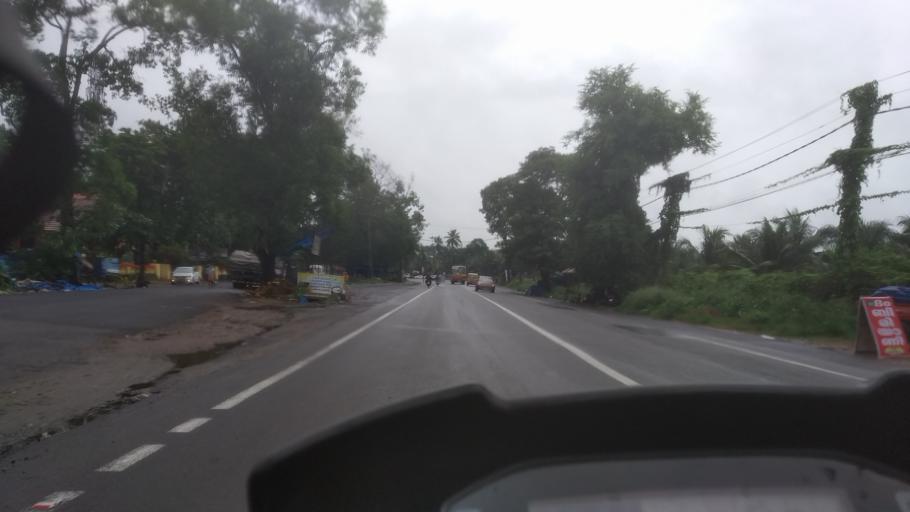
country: IN
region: Kerala
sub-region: Alappuzha
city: Kayankulam
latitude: 9.1485
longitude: 76.5131
